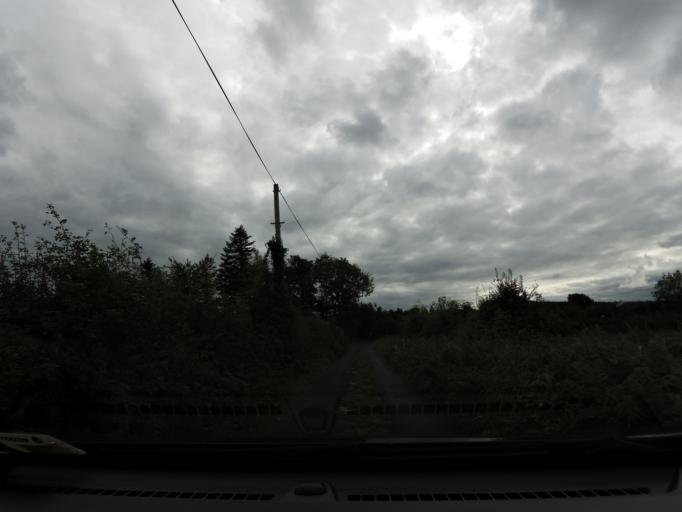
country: IE
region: Connaught
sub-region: County Galway
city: Loughrea
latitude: 53.1513
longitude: -8.4632
